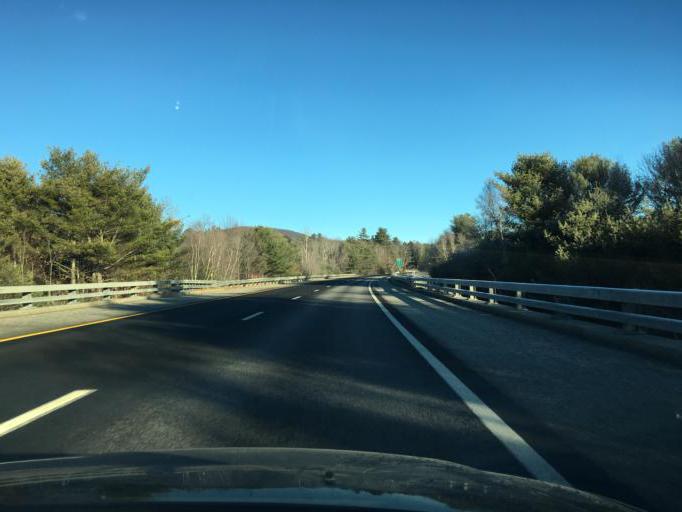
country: US
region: New Hampshire
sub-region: Grafton County
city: Plymouth
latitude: 43.7980
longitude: -71.6765
